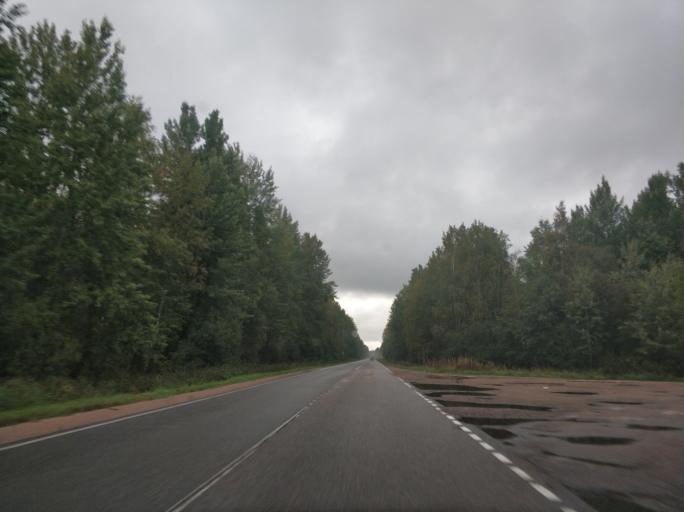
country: RU
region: Leningrad
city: Borisova Griva
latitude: 60.1185
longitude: 30.9636
